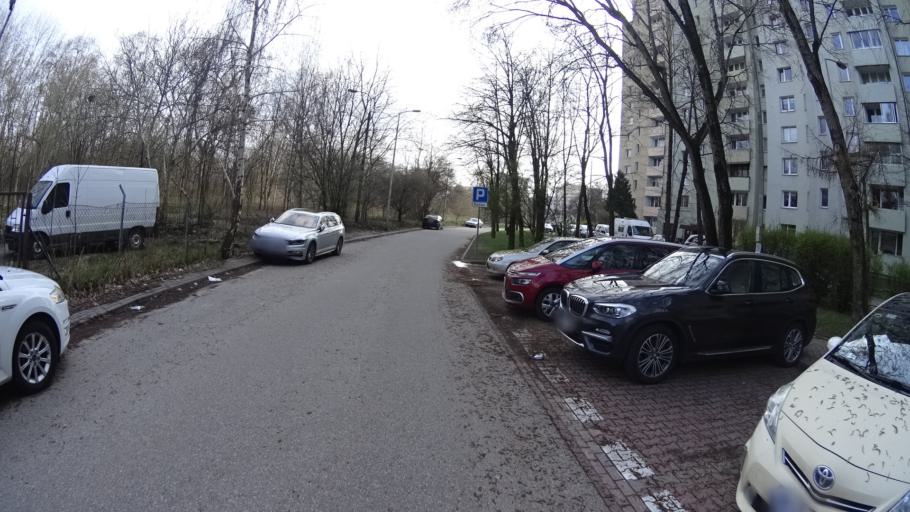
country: PL
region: Masovian Voivodeship
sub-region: Warszawa
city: Bemowo
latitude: 52.2286
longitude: 20.9194
